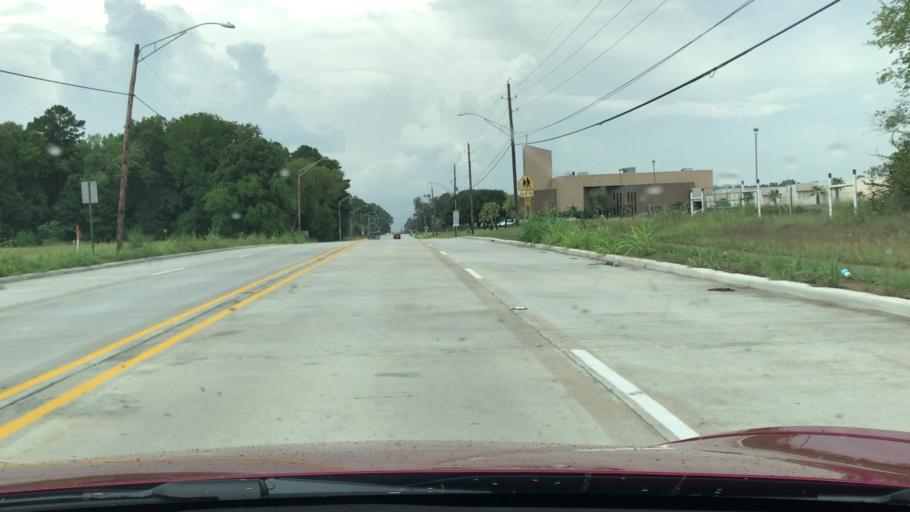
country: US
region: Louisiana
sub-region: Bossier Parish
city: Bossier City
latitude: 32.4016
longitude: -93.7633
